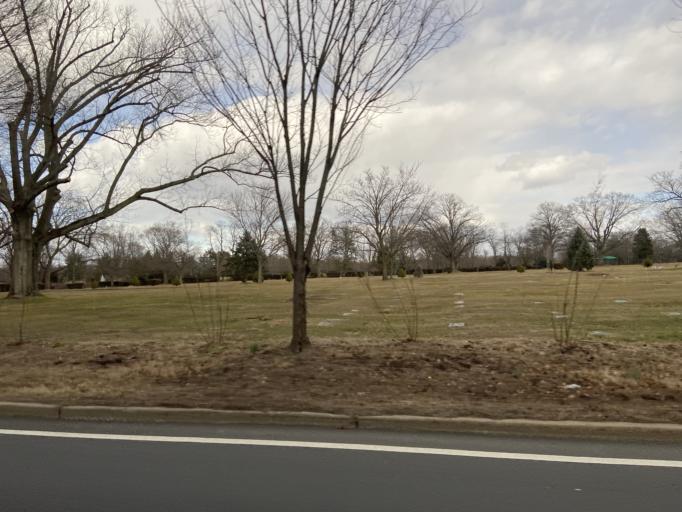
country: US
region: New Jersey
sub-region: Bergen County
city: Paramus
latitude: 40.9430
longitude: -74.0927
